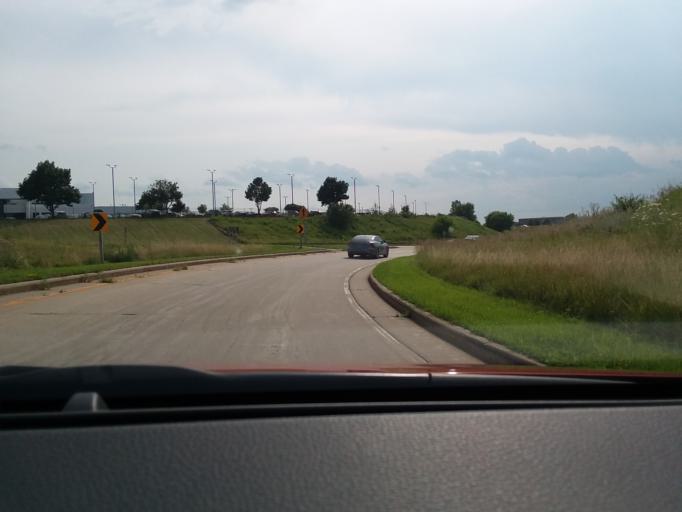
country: US
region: Wisconsin
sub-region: Dane County
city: Sun Prairie
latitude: 43.1452
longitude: -89.2831
